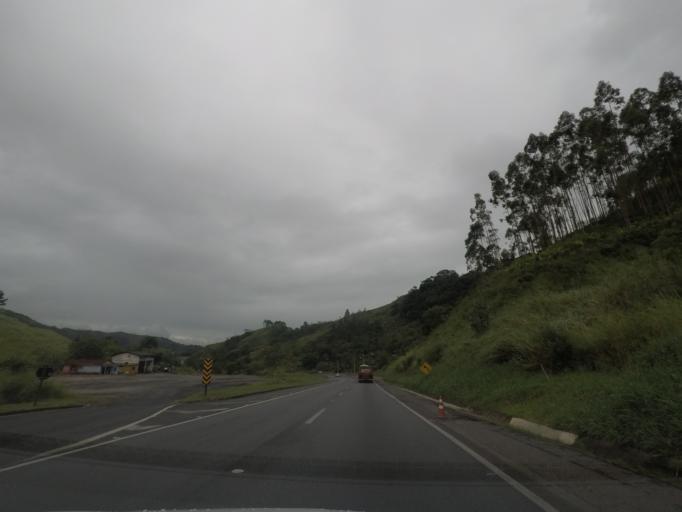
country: BR
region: Sao Paulo
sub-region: Cajati
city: Cajati
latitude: -24.8402
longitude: -48.2132
